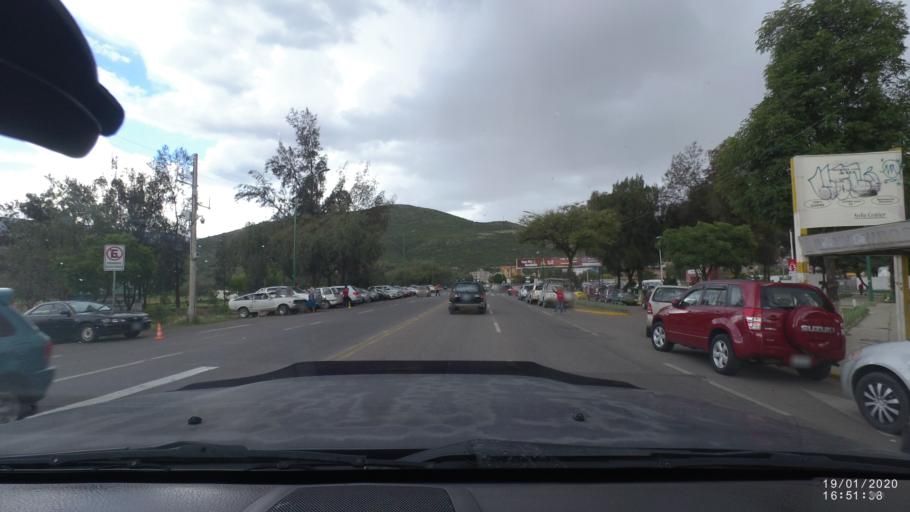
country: BO
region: Cochabamba
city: Cochabamba
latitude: -17.4177
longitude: -66.1300
